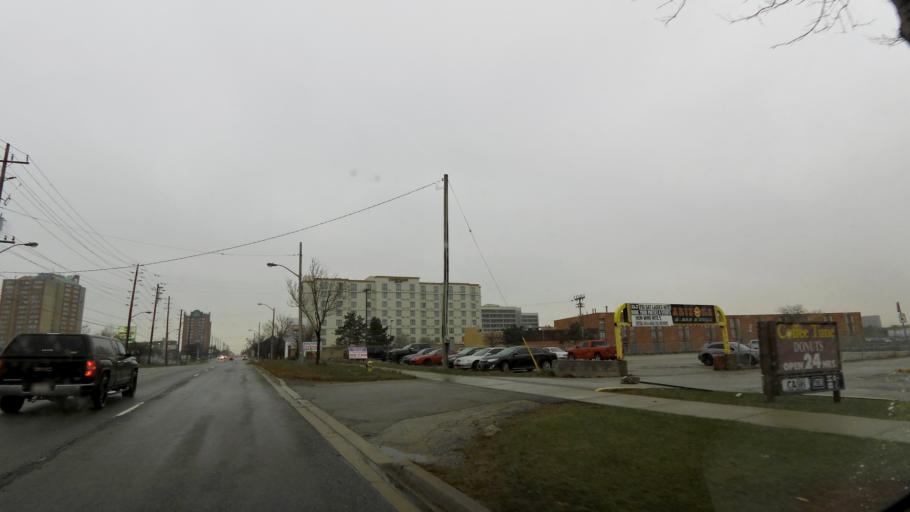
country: CA
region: Ontario
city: Etobicoke
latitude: 43.6836
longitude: -79.5941
